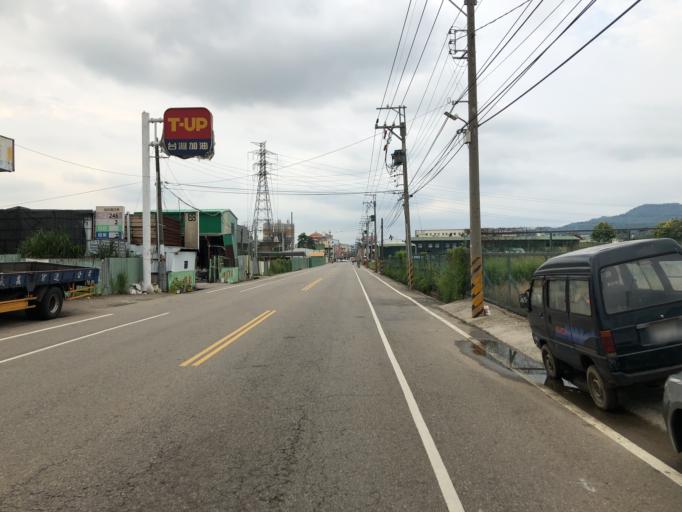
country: TW
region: Taiwan
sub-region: Taichung City
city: Taichung
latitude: 24.0979
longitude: 120.7289
